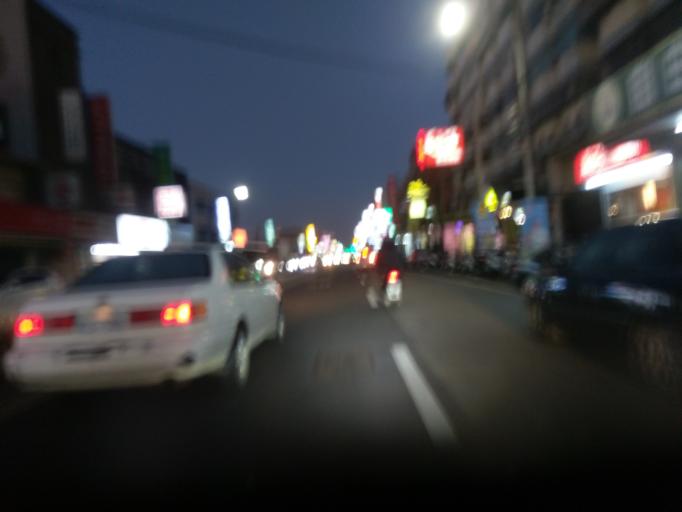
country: TW
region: Taiwan
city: Taoyuan City
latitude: 25.0454
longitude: 121.1405
